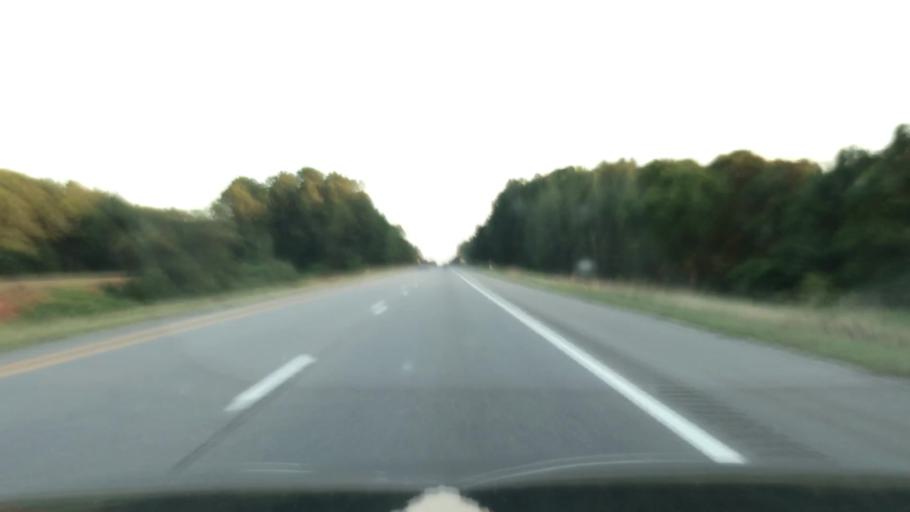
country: US
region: Michigan
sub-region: Montcalm County
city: Howard City
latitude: 43.5168
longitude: -85.4868
